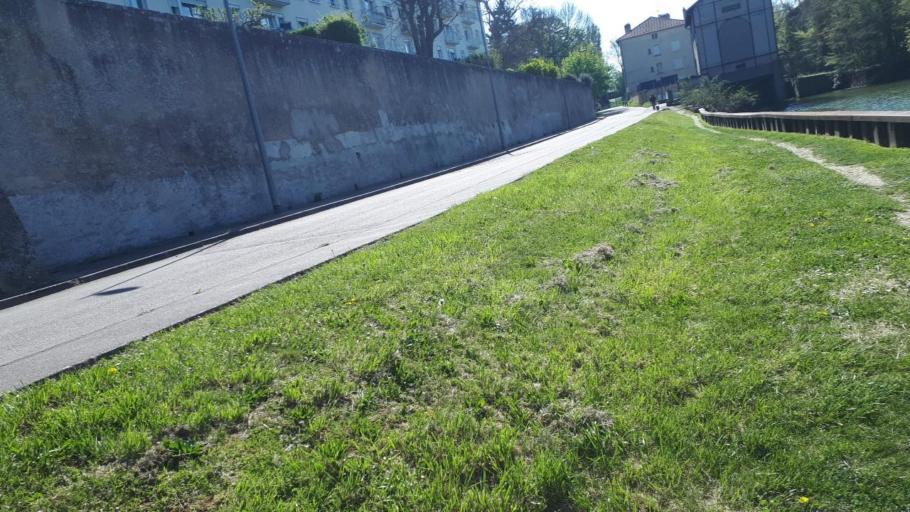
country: FR
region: Lorraine
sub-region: Departement de Meurthe-et-Moselle
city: Tomblaine
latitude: 48.6850
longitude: 6.2099
